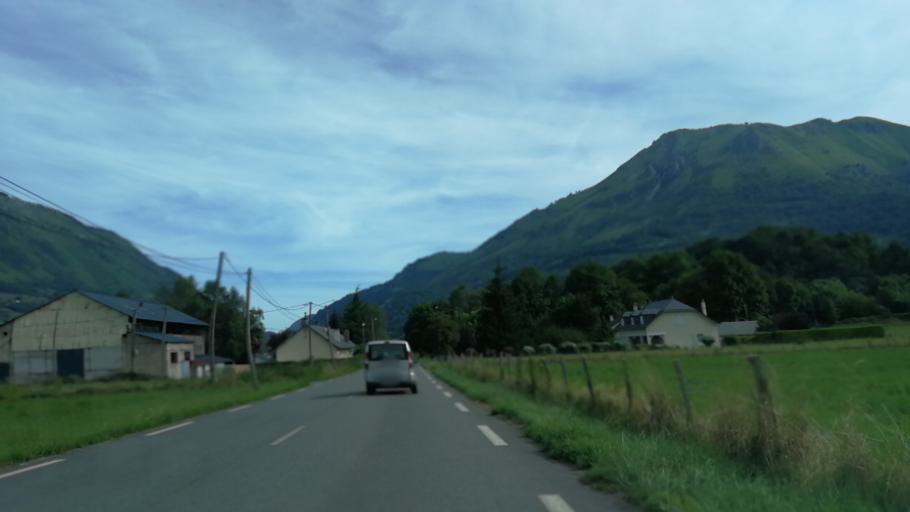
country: FR
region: Aquitaine
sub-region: Departement des Pyrenees-Atlantiques
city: Arette
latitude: 42.9830
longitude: -0.6050
